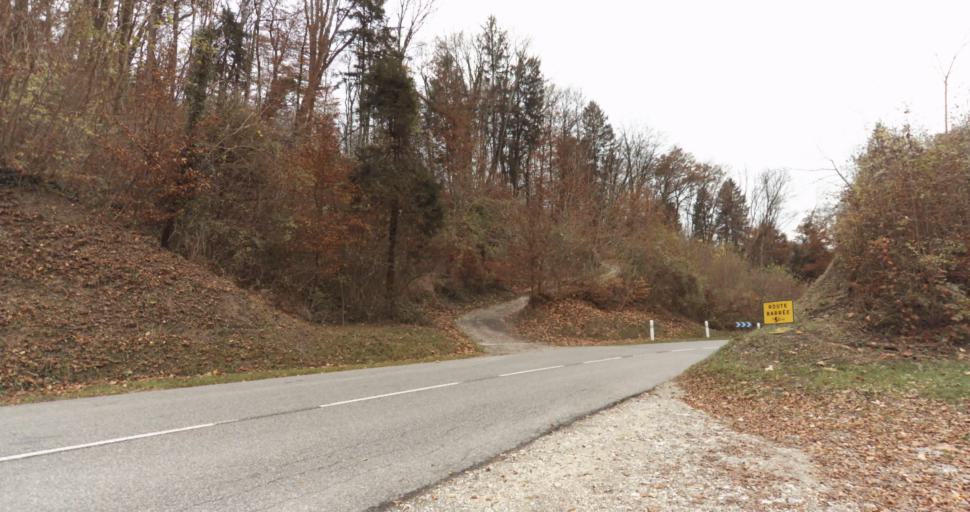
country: FR
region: Rhone-Alpes
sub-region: Departement de la Haute-Savoie
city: Chavanod
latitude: 45.8949
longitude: 6.0380
